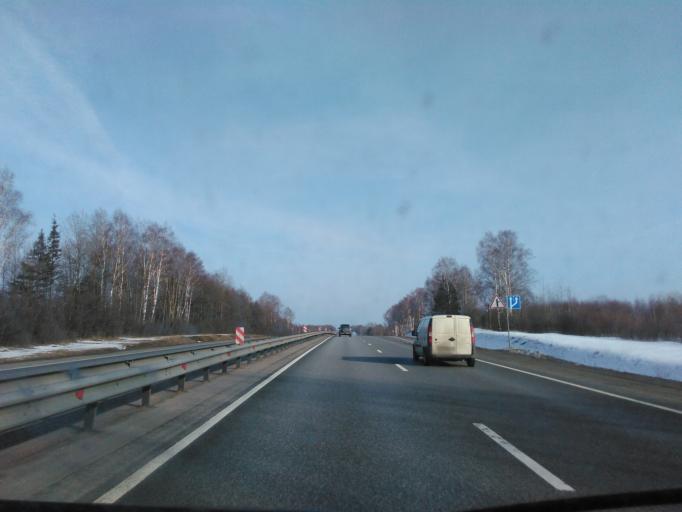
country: RU
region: Smolensk
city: Verkhnedneprovskiy
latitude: 55.1825
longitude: 33.5263
